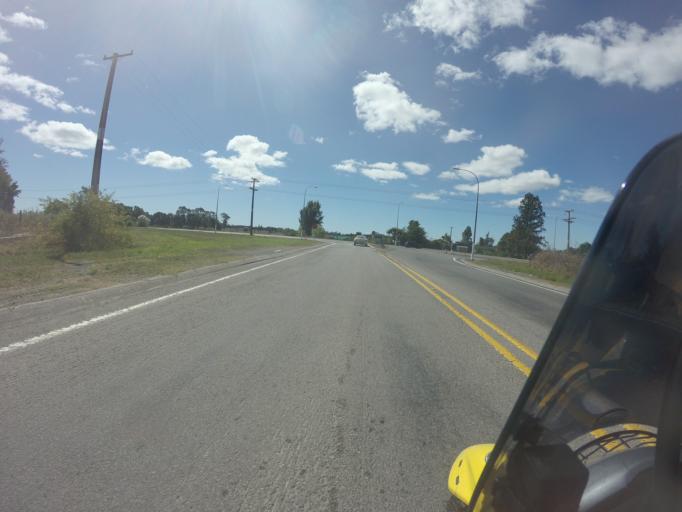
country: NZ
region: Bay of Plenty
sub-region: Whakatane District
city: Edgecumbe
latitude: -37.9978
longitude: 176.8863
